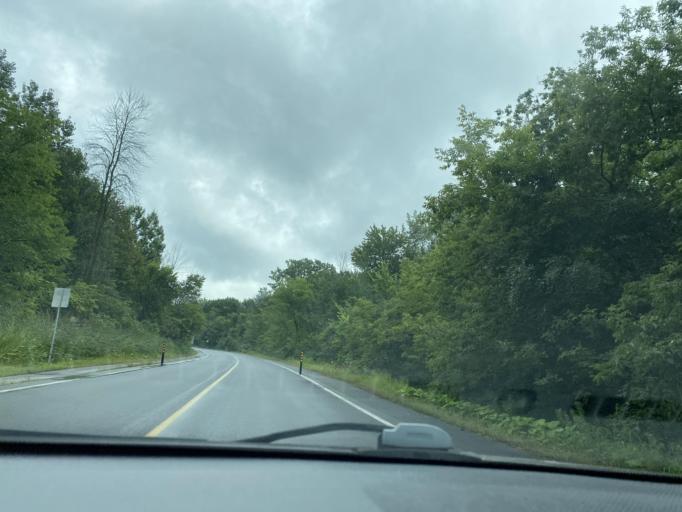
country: CA
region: Quebec
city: Baie-D'Urfe
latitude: 45.4382
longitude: -73.9061
